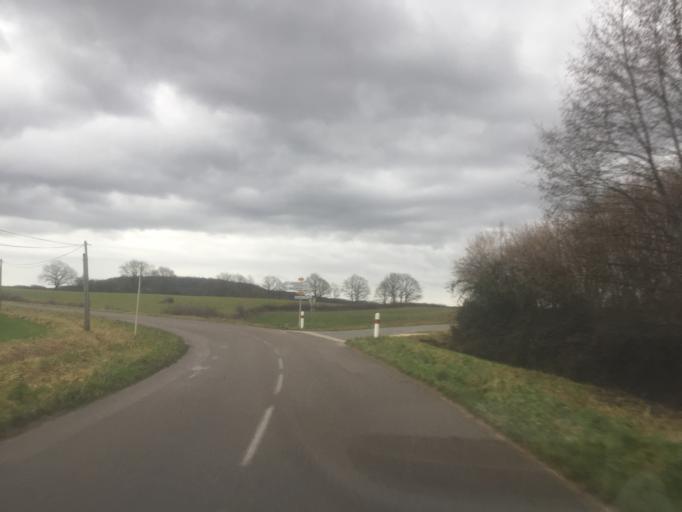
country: FR
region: Franche-Comte
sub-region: Departement de la Haute-Saone
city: Pesmes
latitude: 47.2197
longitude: 5.5022
